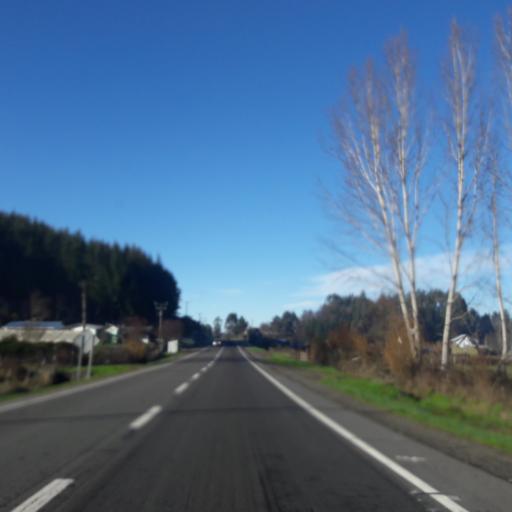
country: CL
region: Biobio
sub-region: Provincia de Biobio
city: La Laja
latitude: -37.2888
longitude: -72.9356
